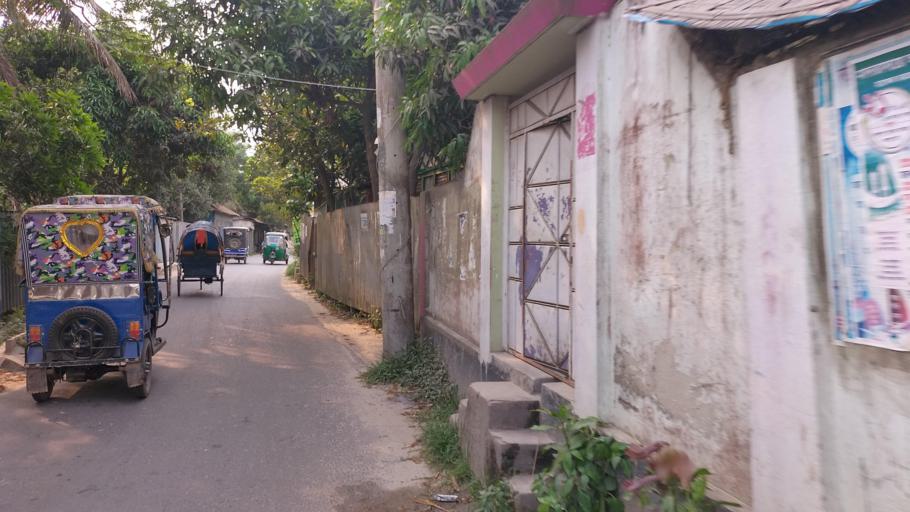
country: BD
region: Dhaka
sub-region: Dhaka
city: Dhaka
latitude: 23.6660
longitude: 90.3505
